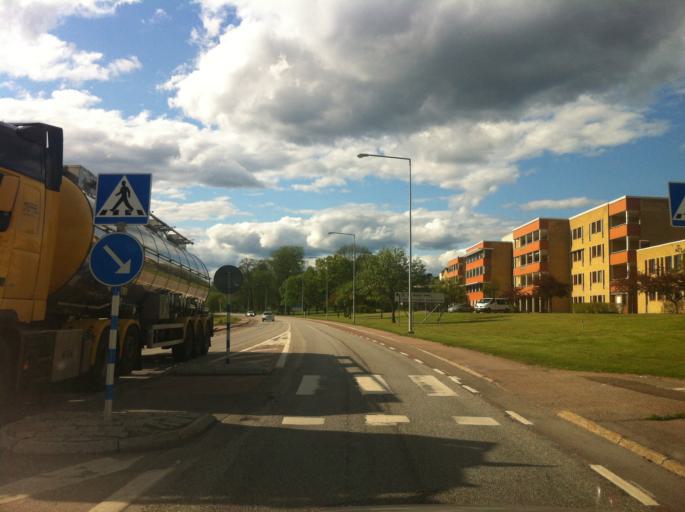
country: SE
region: Vaermland
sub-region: Filipstads Kommun
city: Filipstad
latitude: 59.6974
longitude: 14.1883
